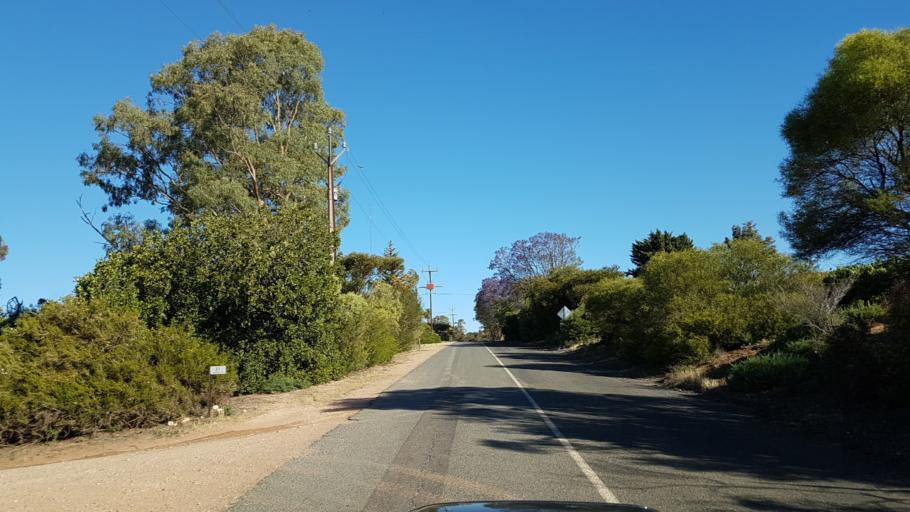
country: AU
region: South Australia
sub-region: Loxton Waikerie
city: Waikerie
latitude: -34.1651
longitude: 140.0346
